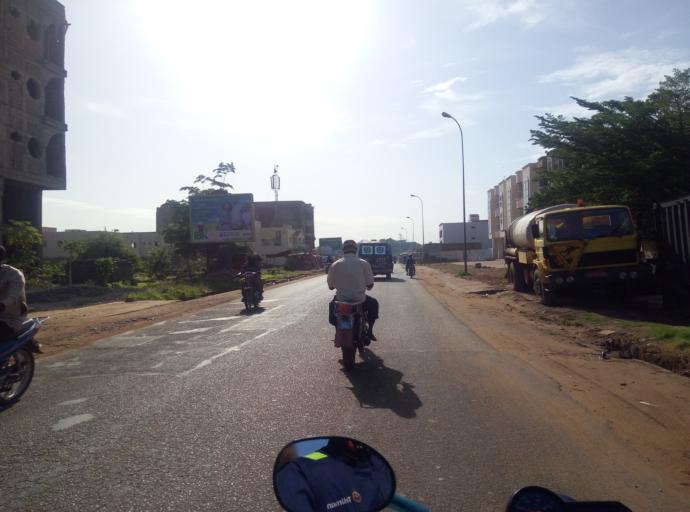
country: ML
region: Bamako
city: Bamako
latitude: 12.6536
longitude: -7.9344
